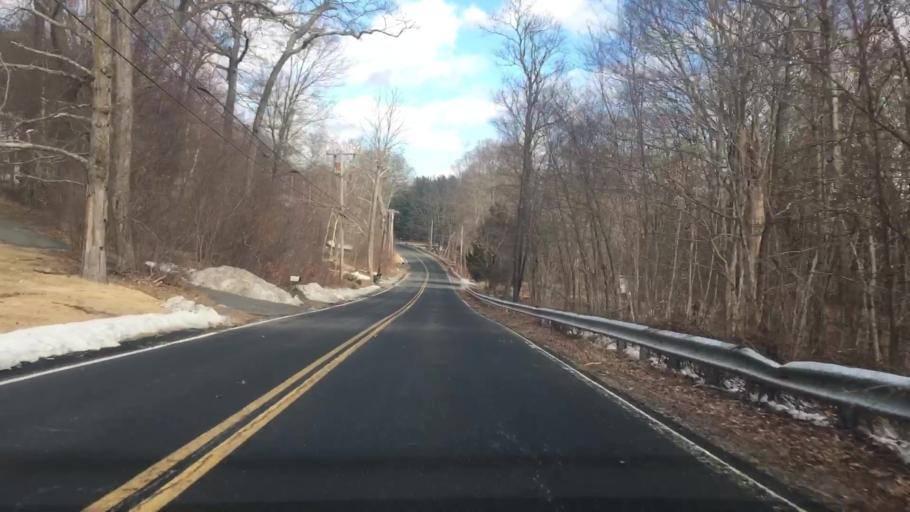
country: US
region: Massachusetts
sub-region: Hampden County
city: Wales
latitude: 42.0523
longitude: -72.2278
